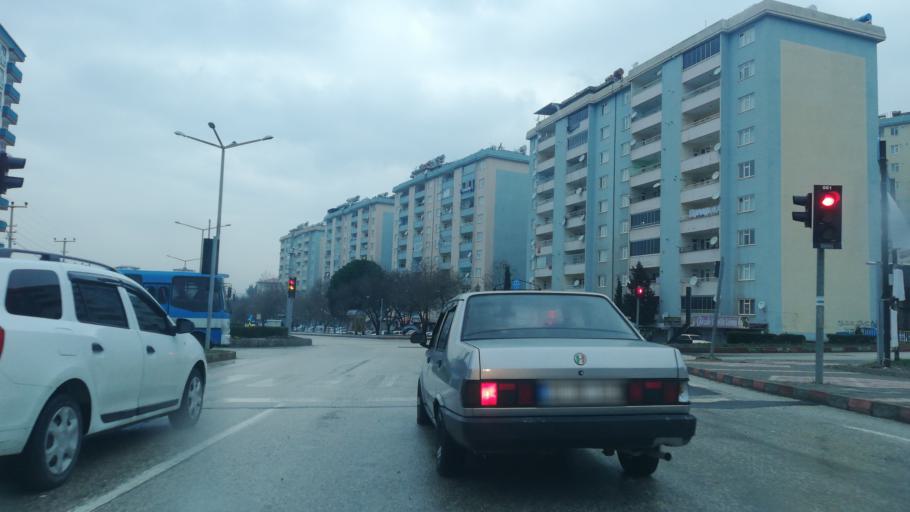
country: TR
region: Kahramanmaras
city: Kahramanmaras
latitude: 37.5833
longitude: 36.9816
